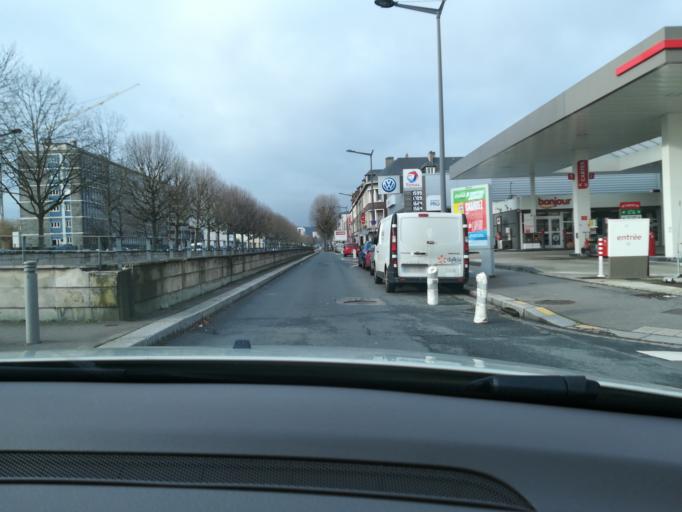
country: FR
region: Haute-Normandie
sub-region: Departement de la Seine-Maritime
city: Rouen
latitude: 49.4439
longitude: 1.0762
